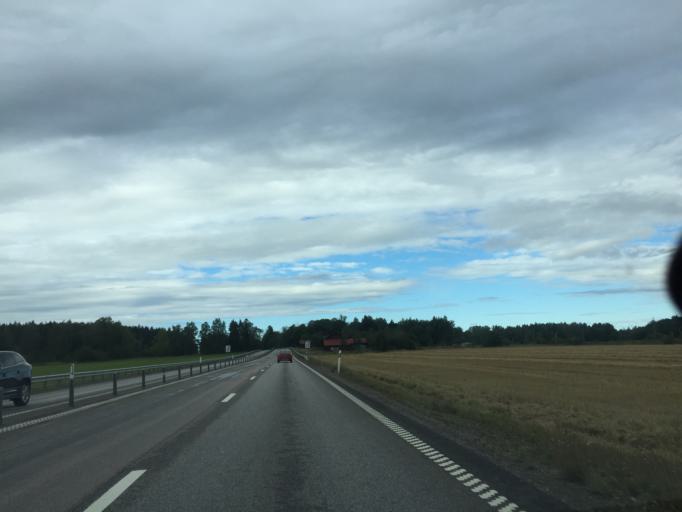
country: SE
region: Soedermanland
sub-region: Eskilstuna Kommun
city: Kvicksund
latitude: 59.4117
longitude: 16.2262
